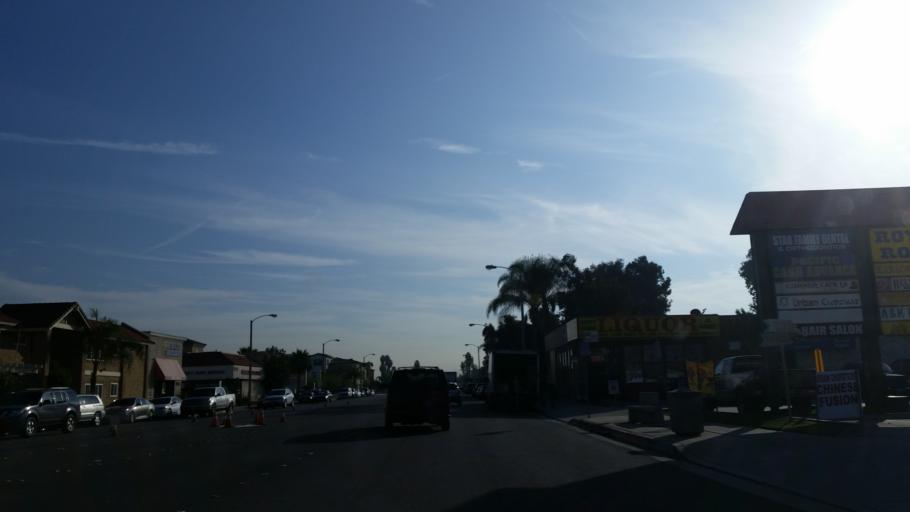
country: US
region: California
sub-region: Los Angeles County
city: Paramount
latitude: 33.8892
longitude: -118.1383
